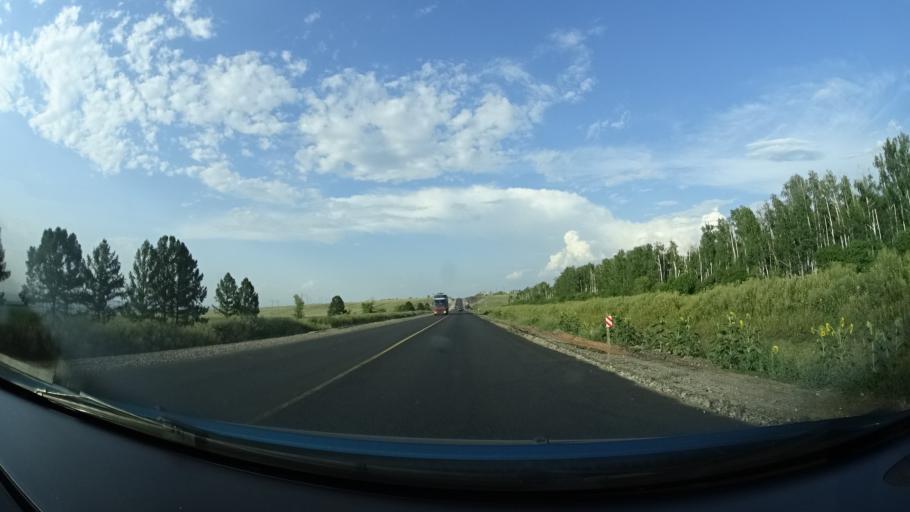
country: RU
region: Samara
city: Sukhodol
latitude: 53.7259
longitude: 50.8344
